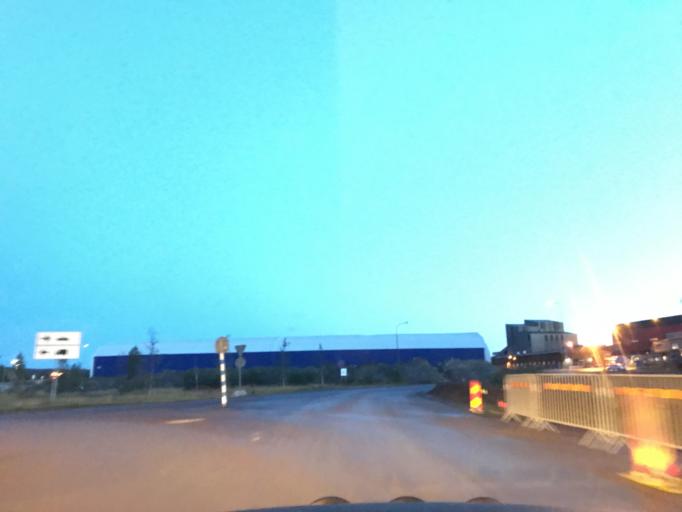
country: SE
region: Norrbotten
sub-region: Gallivare Kommun
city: Malmberget
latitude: 67.6400
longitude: 21.0172
